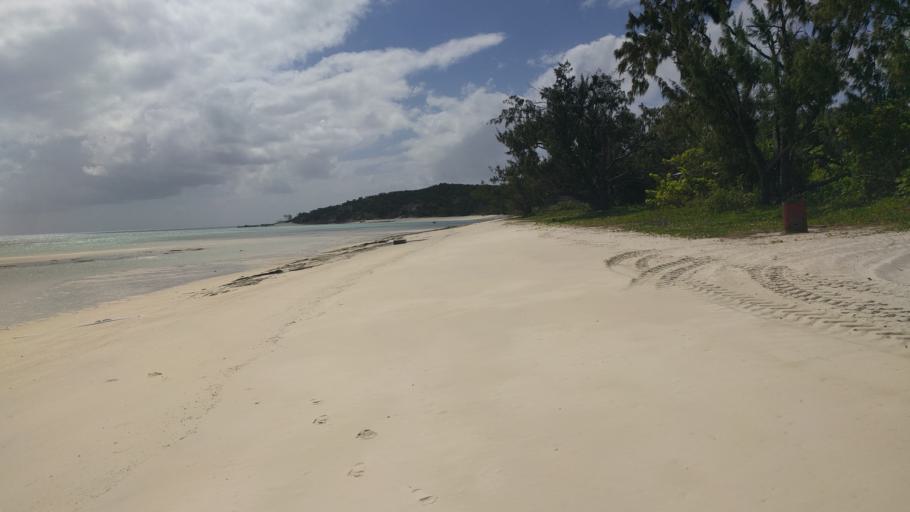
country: AU
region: Queensland
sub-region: Cook
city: Cooktown
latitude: -14.6792
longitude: 145.4475
